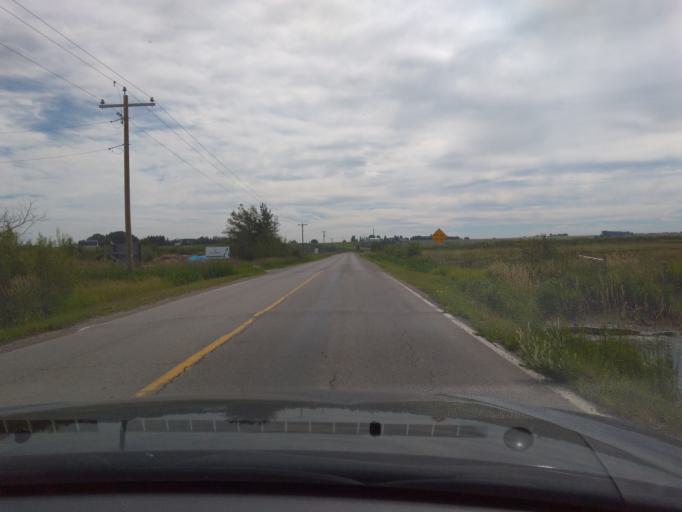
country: CA
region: Alberta
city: Didsbury
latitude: 51.6568
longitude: -114.1104
